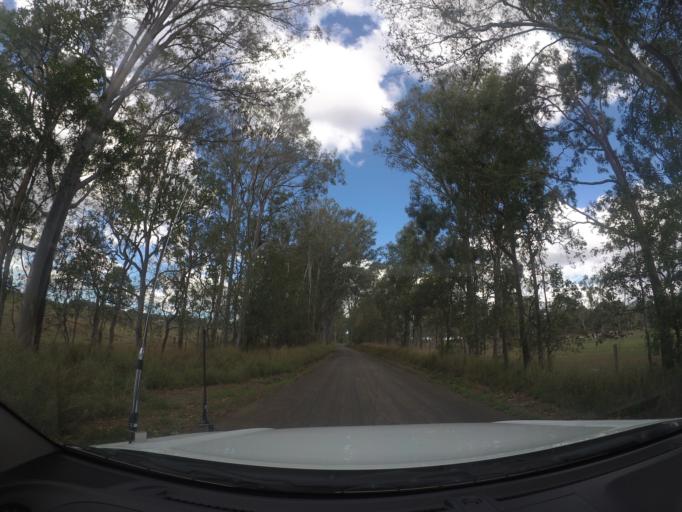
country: AU
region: Queensland
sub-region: Logan
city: Cedar Vale
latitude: -27.8935
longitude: 152.9672
